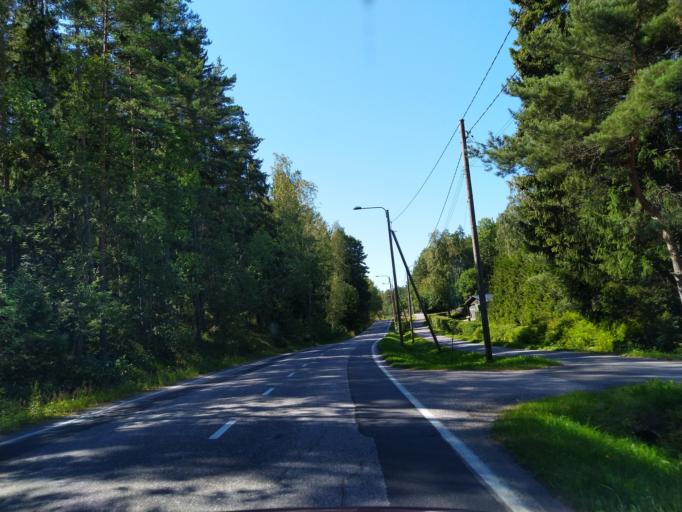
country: FI
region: Varsinais-Suomi
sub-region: Aboland-Turunmaa
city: Dragsfjaerd
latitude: 60.0190
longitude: 22.4896
